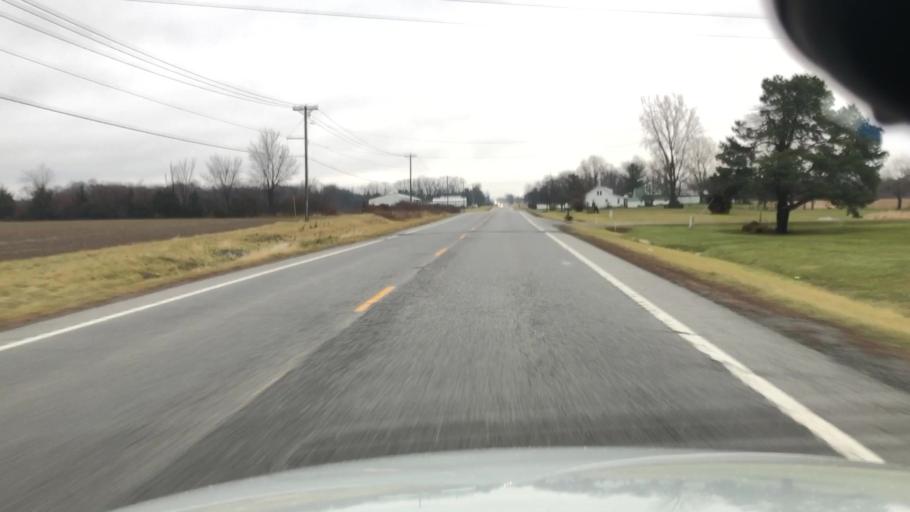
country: US
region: Ohio
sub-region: Allen County
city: Lima
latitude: 40.7311
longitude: -84.0072
